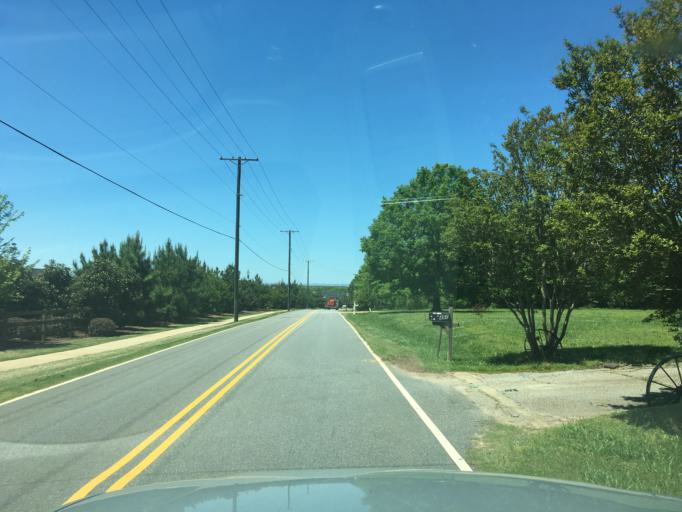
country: US
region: South Carolina
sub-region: Spartanburg County
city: Duncan
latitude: 34.8599
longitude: -82.1483
